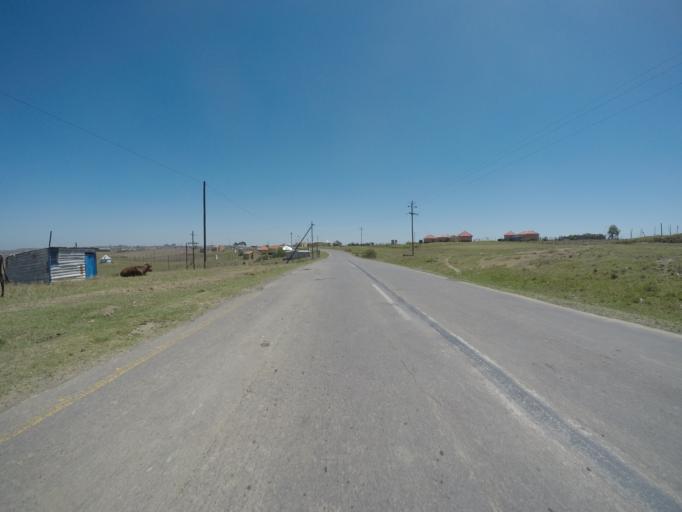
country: ZA
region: Eastern Cape
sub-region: OR Tambo District Municipality
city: Libode
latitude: -31.9109
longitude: 29.0187
